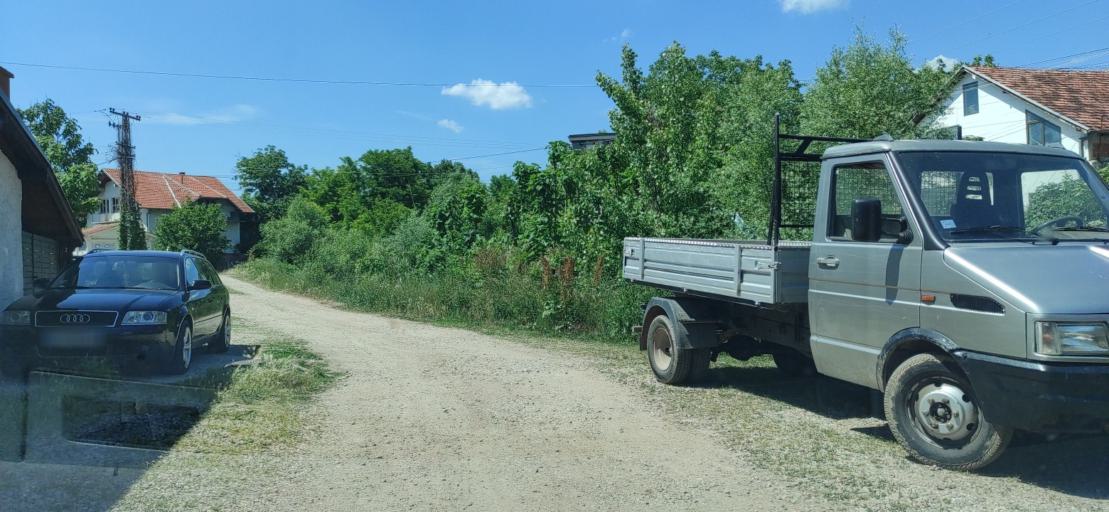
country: RS
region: Central Serbia
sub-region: Nisavski Okrug
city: Nis
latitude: 43.3279
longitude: 21.9514
